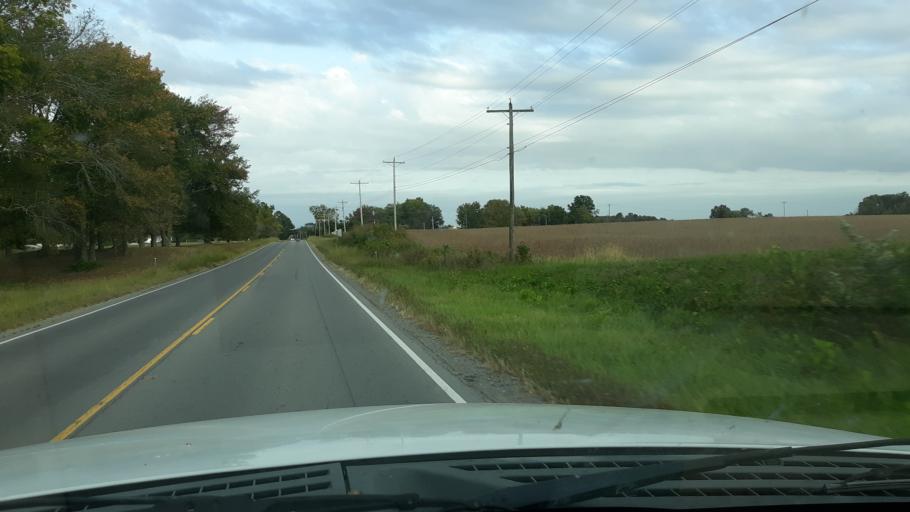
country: US
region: Illinois
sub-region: Saline County
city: Eldorado
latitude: 37.8214
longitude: -88.4897
